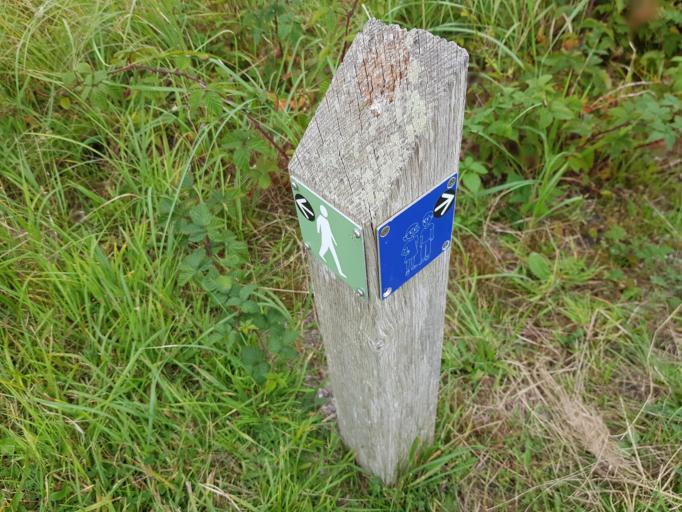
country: NL
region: North Holland
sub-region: Gemeente Texel
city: Den Burg
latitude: 53.0764
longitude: 4.7447
